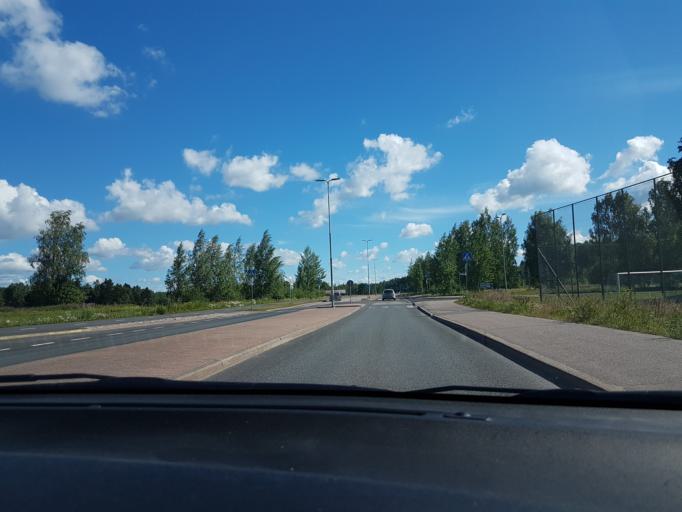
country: FI
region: Uusimaa
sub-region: Helsinki
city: Kerava
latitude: 60.3591
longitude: 25.0799
